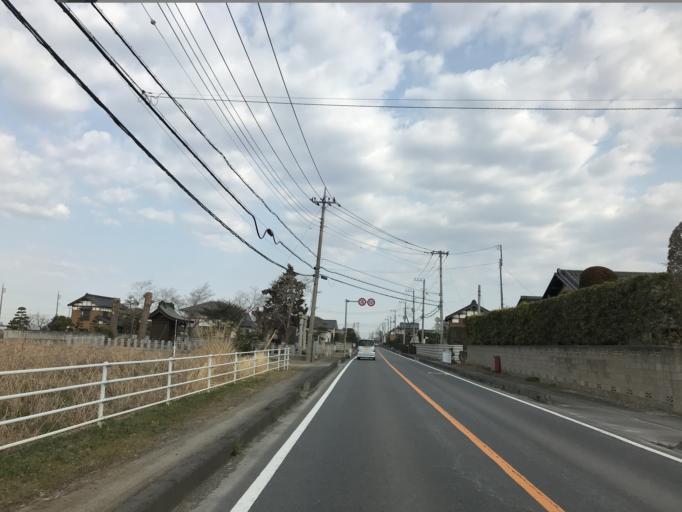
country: JP
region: Ibaraki
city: Mitsukaido
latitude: 35.9964
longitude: 140.0161
